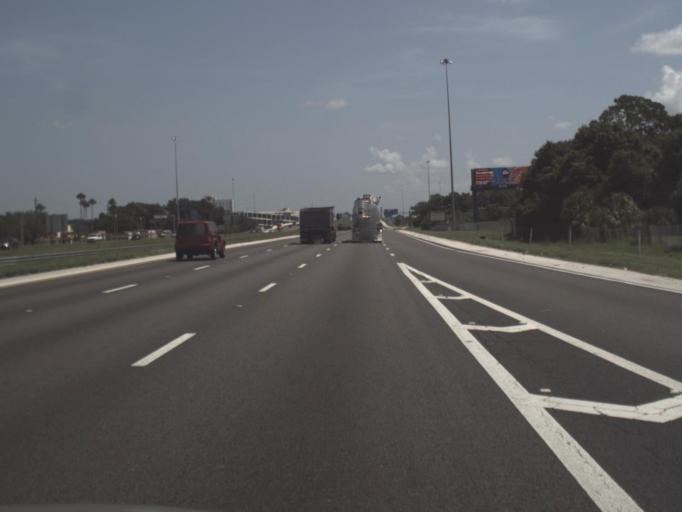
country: US
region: Florida
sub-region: Hillsborough County
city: East Lake-Orient Park
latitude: 27.9843
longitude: -82.3802
